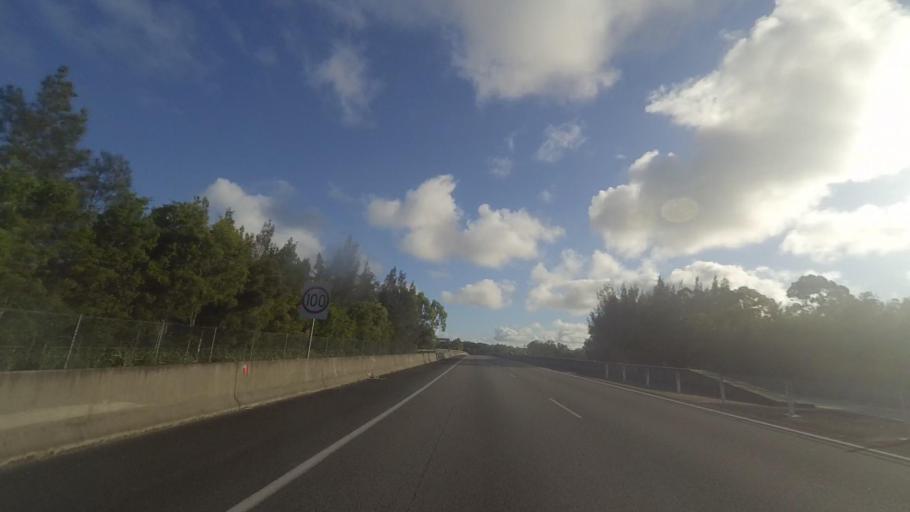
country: AU
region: New South Wales
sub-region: Great Lakes
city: Nabiac
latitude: -32.1038
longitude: 152.3746
